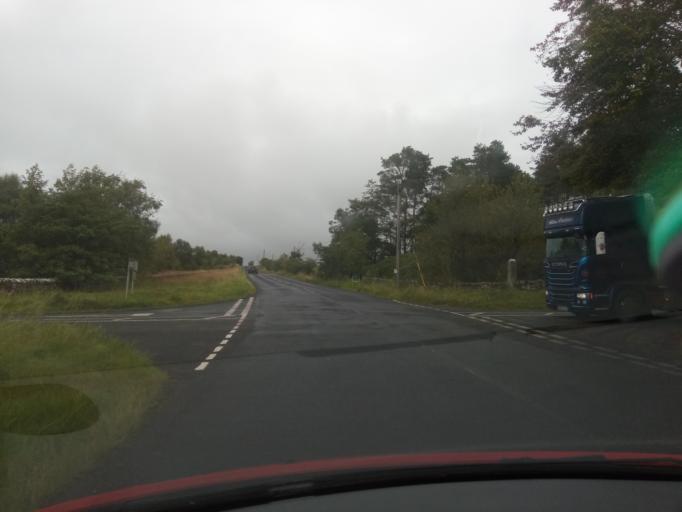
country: GB
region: England
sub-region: Northumberland
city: Rothley
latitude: 55.2011
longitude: -1.9330
